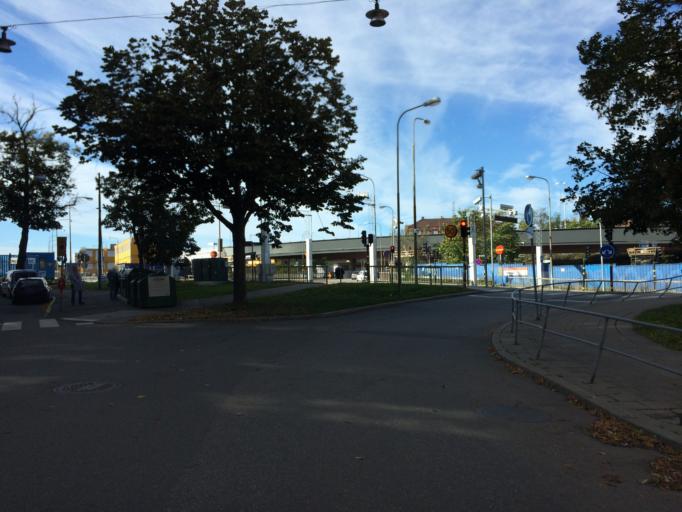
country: SE
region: Stockholm
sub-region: Solna Kommun
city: Solna
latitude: 59.3432
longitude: 18.0279
